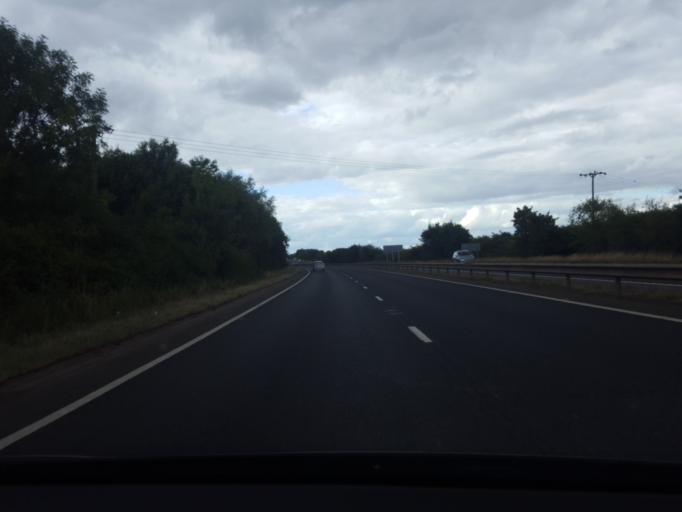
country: GB
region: England
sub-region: Leicestershire
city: Mountsorrel
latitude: 52.7263
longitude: -1.1296
